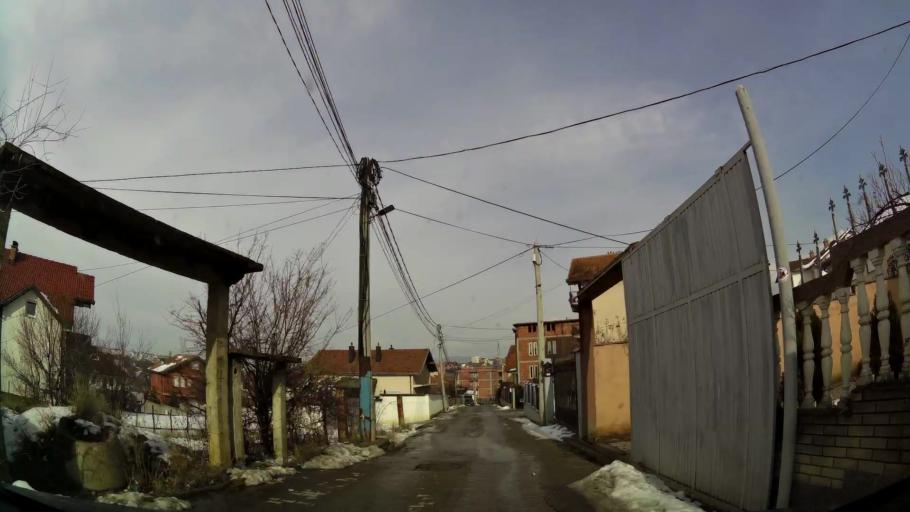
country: XK
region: Pristina
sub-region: Komuna e Prishtines
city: Pristina
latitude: 42.6915
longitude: 21.1580
